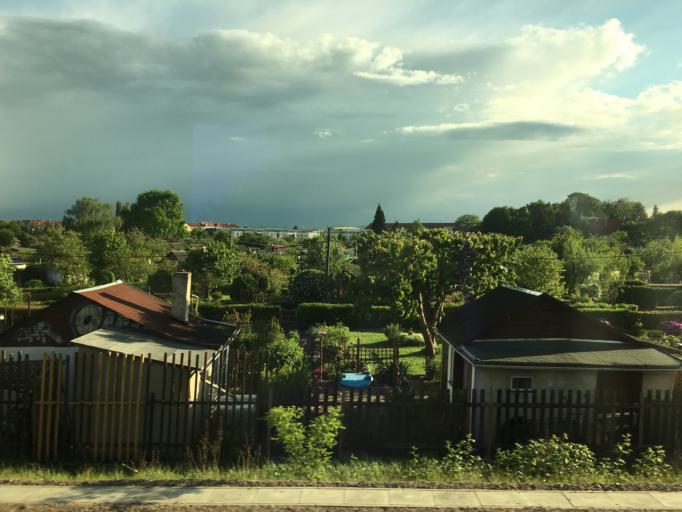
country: DE
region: Saxony
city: Dresden
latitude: 51.0854
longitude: 13.7190
